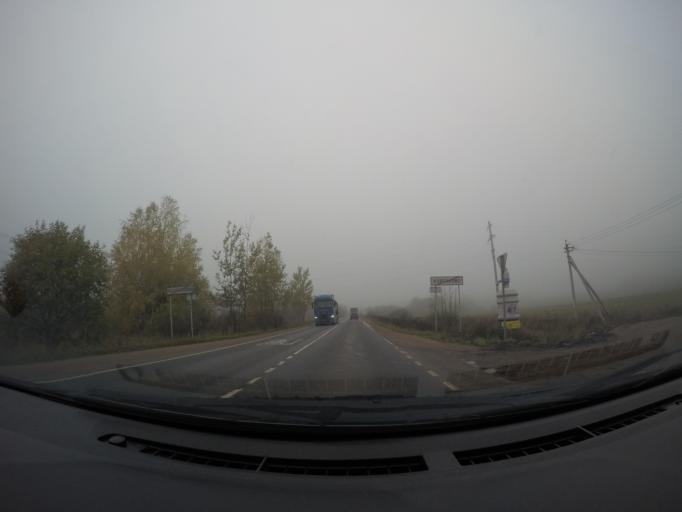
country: RU
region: Moskovskaya
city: Kostrovo
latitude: 55.8685
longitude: 36.5906
